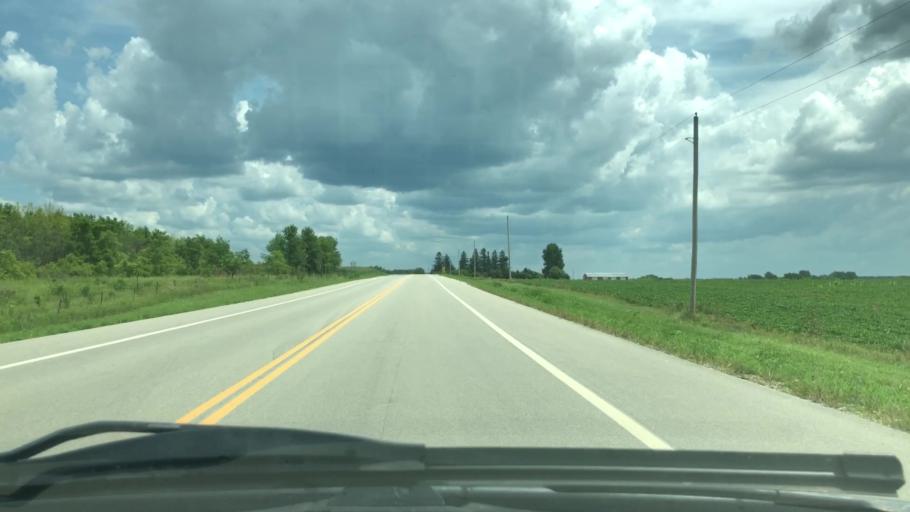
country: US
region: Minnesota
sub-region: Olmsted County
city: Rochester
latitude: 43.9496
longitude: -92.5259
